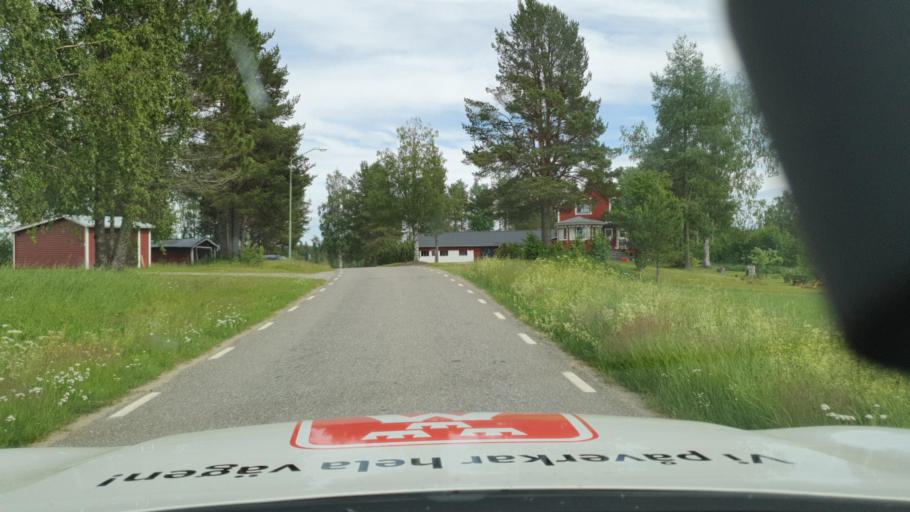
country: SE
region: Vaesterbotten
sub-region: Skelleftea Kommun
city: Burtraesk
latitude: 64.4973
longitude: 20.8637
